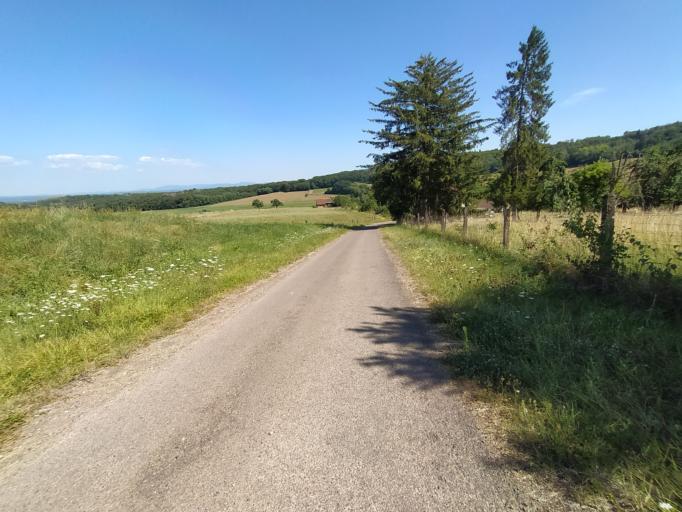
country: FR
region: Franche-Comte
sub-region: Departement de la Haute-Saone
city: Luxeuil-les-Bains
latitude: 47.7548
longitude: 6.3127
